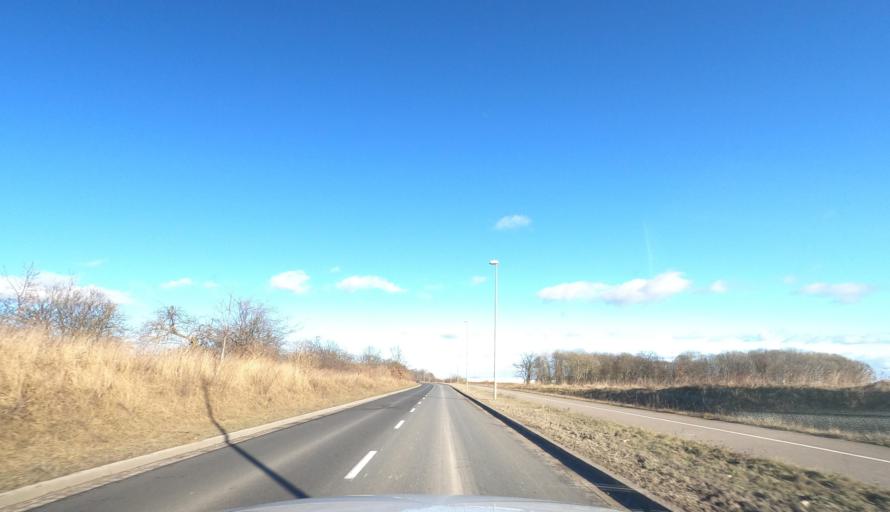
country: PL
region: West Pomeranian Voivodeship
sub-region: Powiat pyrzycki
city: Warnice
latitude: 53.2969
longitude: 14.9612
